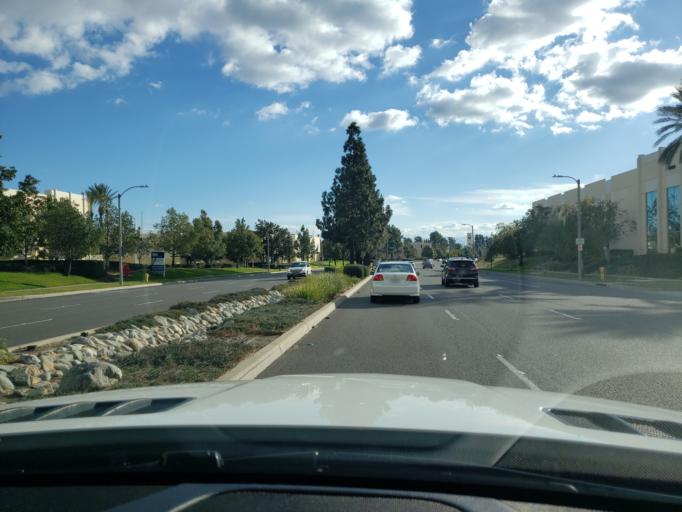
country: US
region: California
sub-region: San Bernardino County
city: Rancho Cucamonga
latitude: 34.0969
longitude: -117.5558
